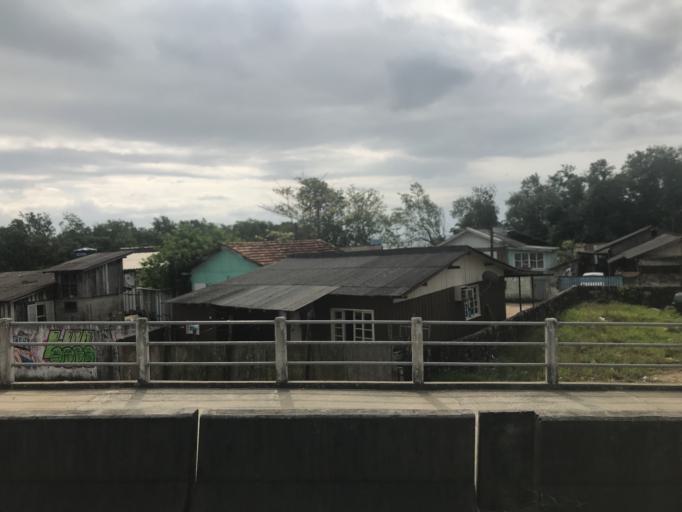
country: BR
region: Santa Catarina
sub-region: Florianopolis
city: Costeira do Pirajubae
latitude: -27.6509
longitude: -48.5227
